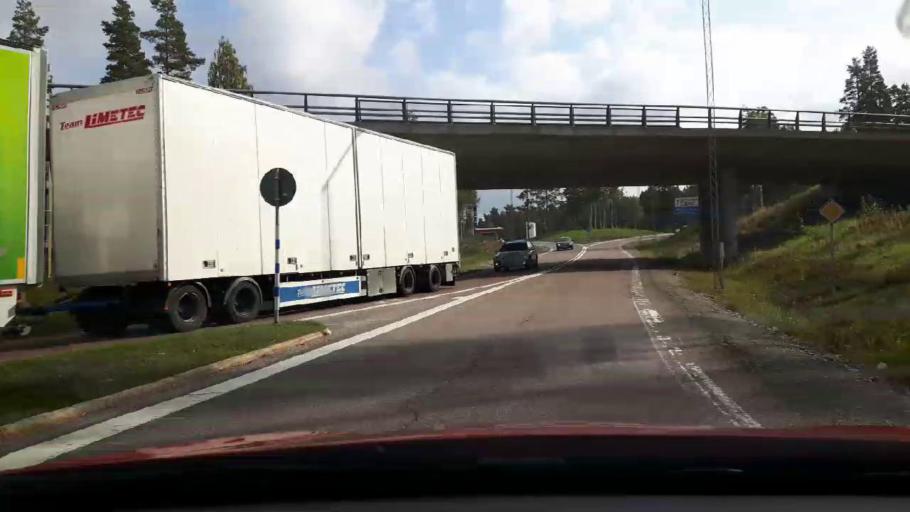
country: SE
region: Gaevleborg
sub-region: Gavle Kommun
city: Norrsundet
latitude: 61.0727
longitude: 16.9636
